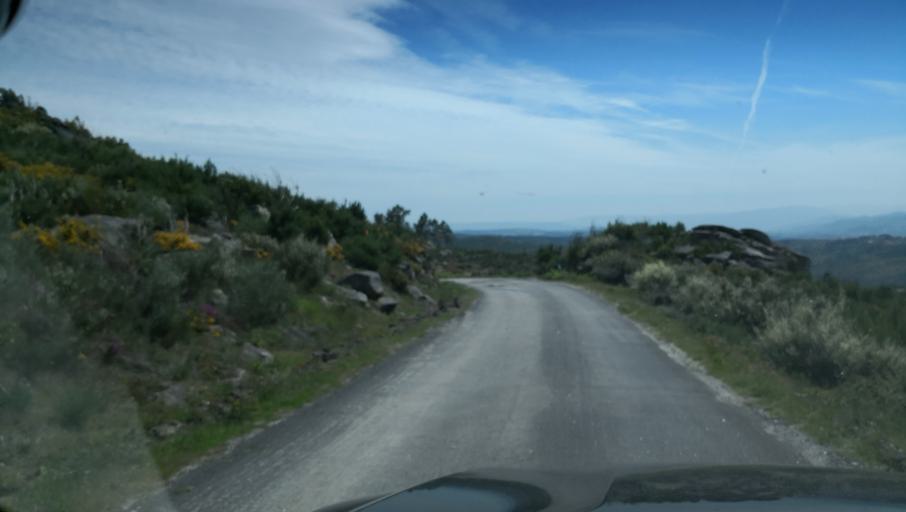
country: PT
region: Vila Real
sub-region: Vila Real
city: Vila Real
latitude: 41.3685
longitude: -7.6998
